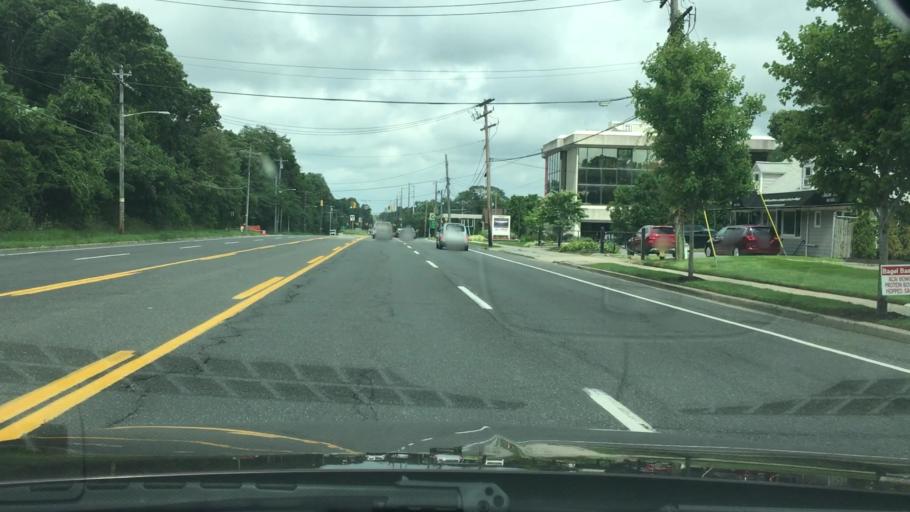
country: US
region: New York
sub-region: Suffolk County
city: Commack
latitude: 40.8132
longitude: -73.2940
